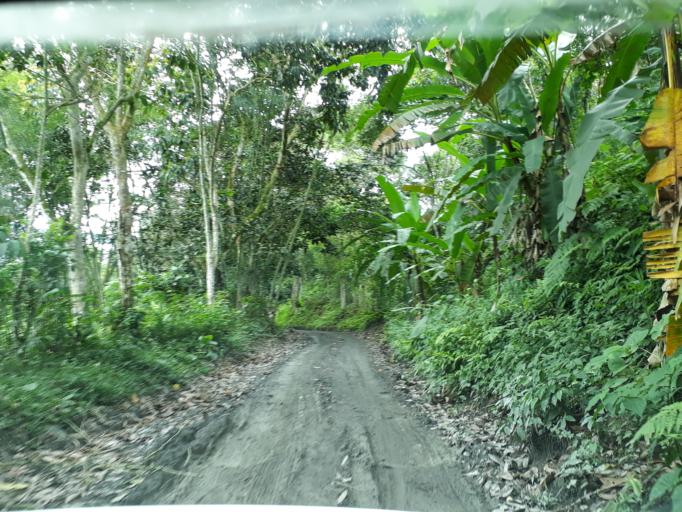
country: CO
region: Boyaca
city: Quipama
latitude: 5.4566
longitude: -74.1762
